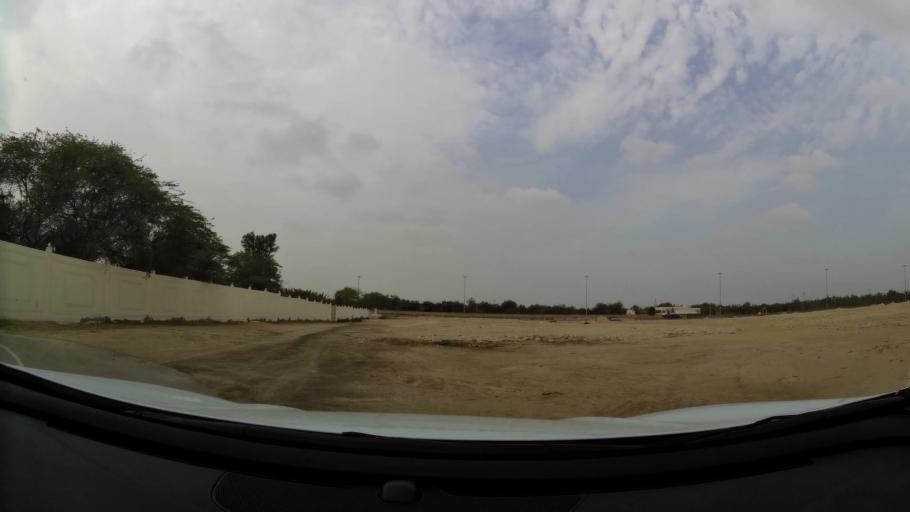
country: AE
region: Abu Dhabi
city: Abu Dhabi
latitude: 24.6225
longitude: 54.7058
